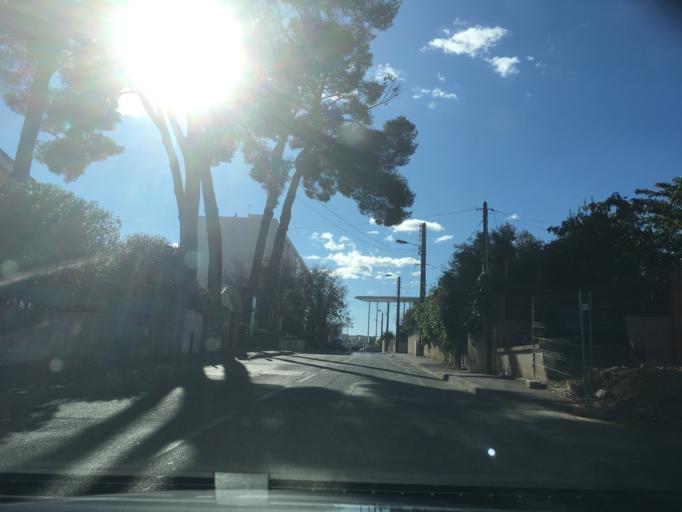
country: FR
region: Languedoc-Roussillon
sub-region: Departement de l'Herault
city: Montpellier
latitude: 43.5943
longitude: 3.8532
